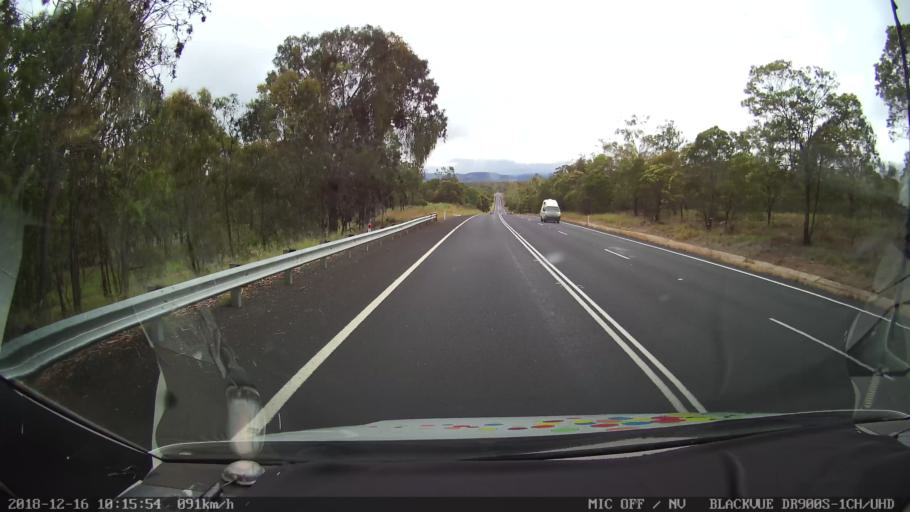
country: AU
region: New South Wales
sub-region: Tenterfield Municipality
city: Carrolls Creek
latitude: -29.2726
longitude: 151.9769
